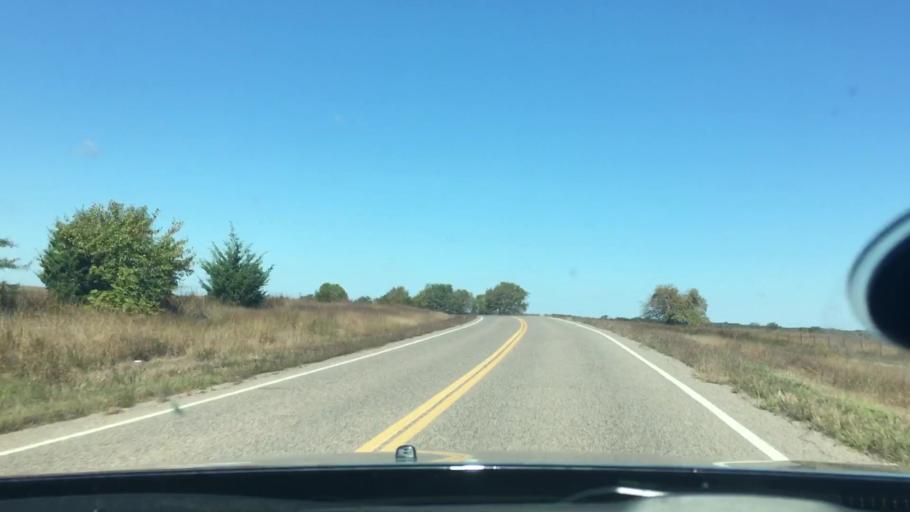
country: US
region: Oklahoma
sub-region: Johnston County
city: Tishomingo
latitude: 34.1625
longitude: -96.7063
